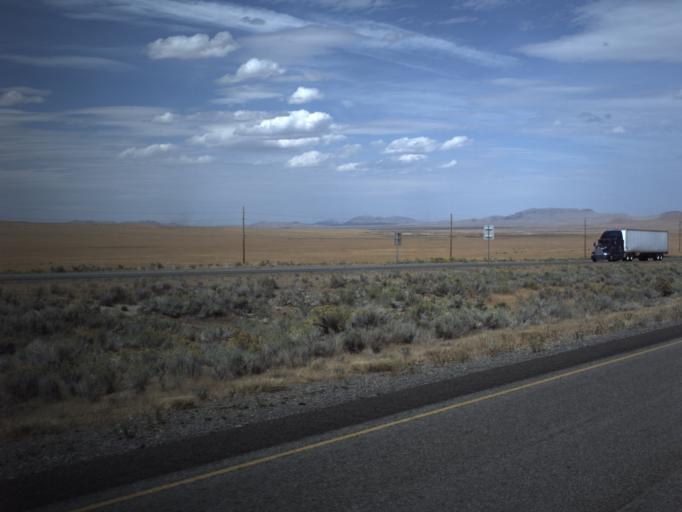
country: US
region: Utah
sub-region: Tooele County
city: Grantsville
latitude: 40.7707
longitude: -112.9804
